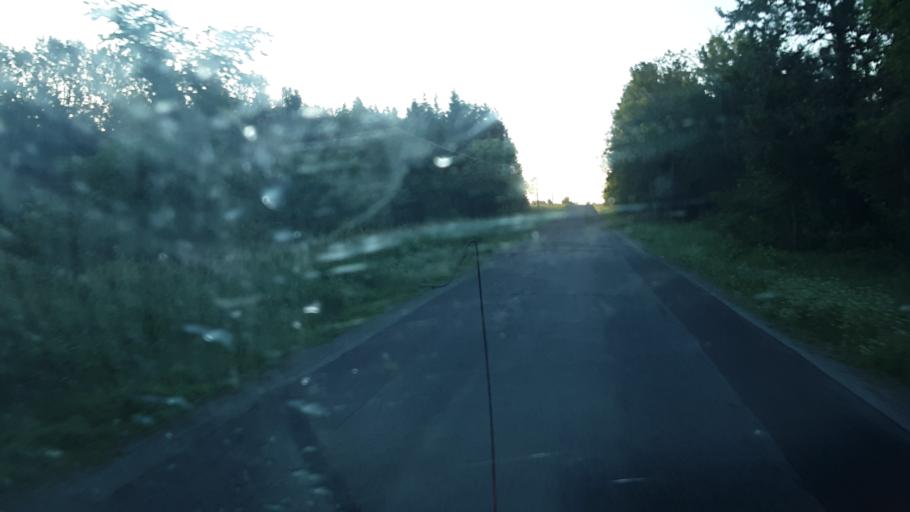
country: US
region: Maine
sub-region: Aroostook County
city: Caribou
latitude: 46.8028
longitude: -68.1062
